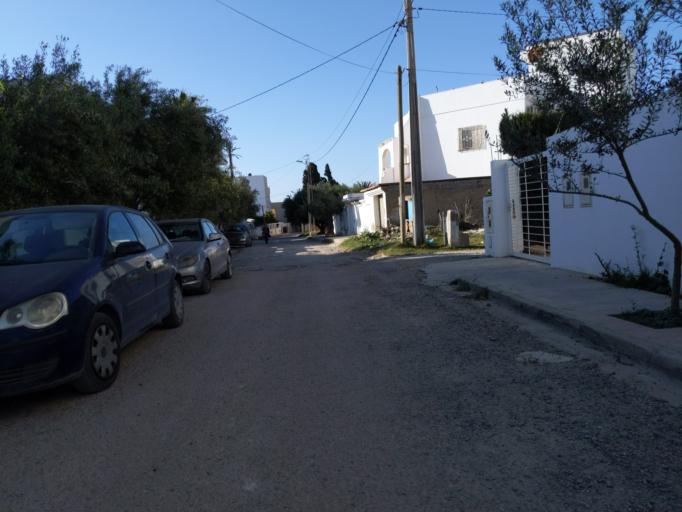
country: TN
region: Al Munastir
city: Saqanis
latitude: 35.7766
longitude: 10.7985
